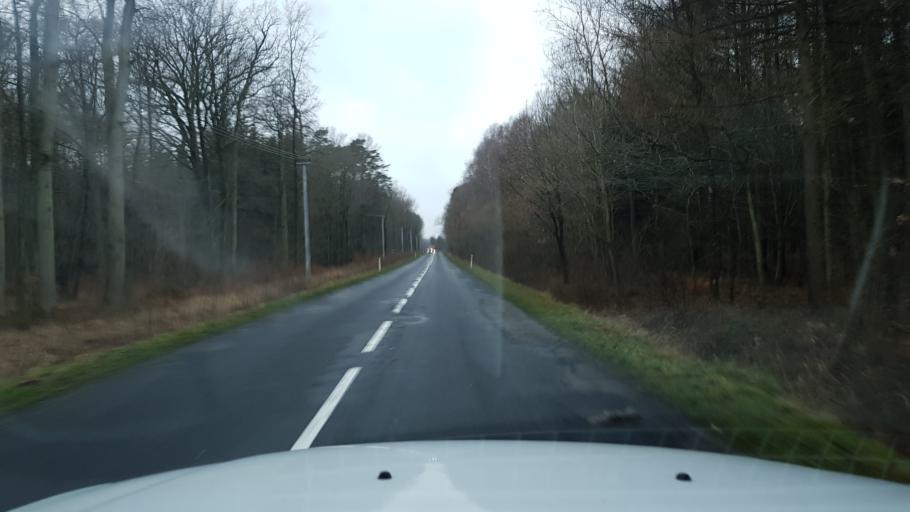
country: PL
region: West Pomeranian Voivodeship
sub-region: Powiat gryficki
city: Trzebiatow
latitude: 54.0573
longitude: 15.3381
